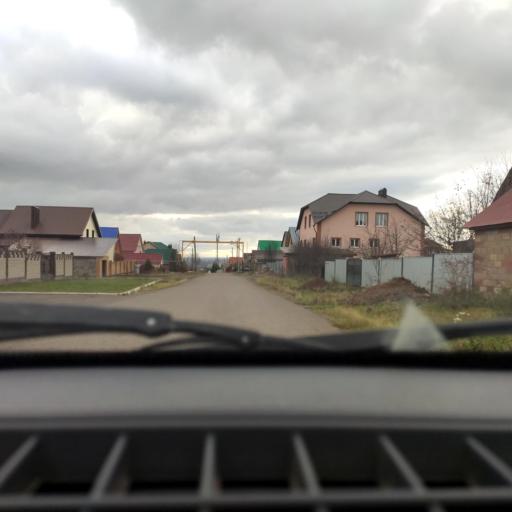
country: RU
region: Bashkortostan
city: Mikhaylovka
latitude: 54.8183
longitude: 55.8901
